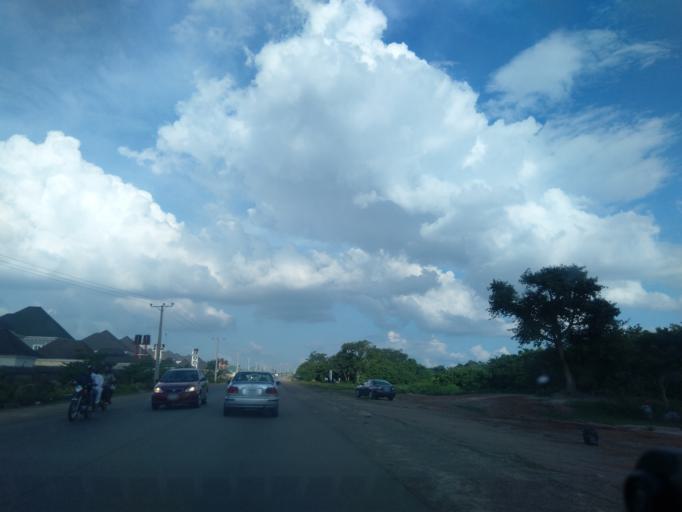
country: NG
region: Abuja Federal Capital Territory
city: Abuja
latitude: 9.0422
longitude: 7.3919
